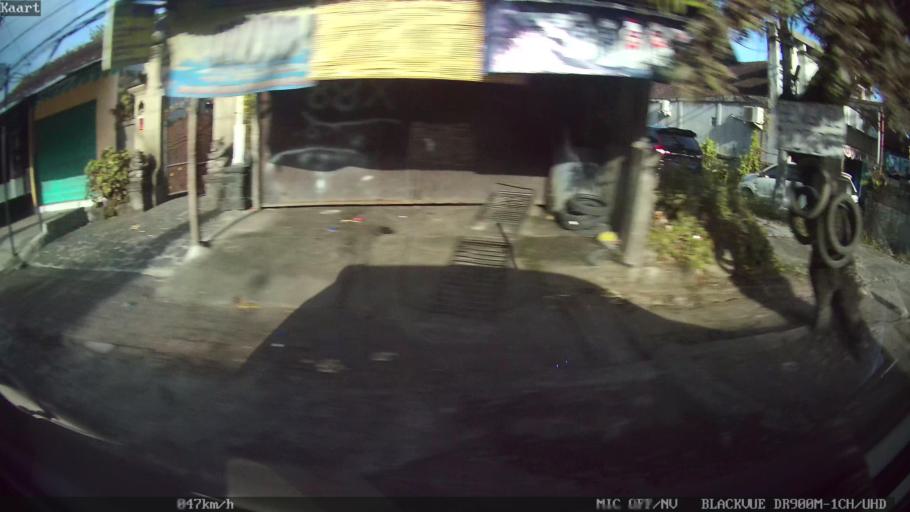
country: ID
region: Bali
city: Banjar Batur
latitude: -8.5934
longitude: 115.2153
